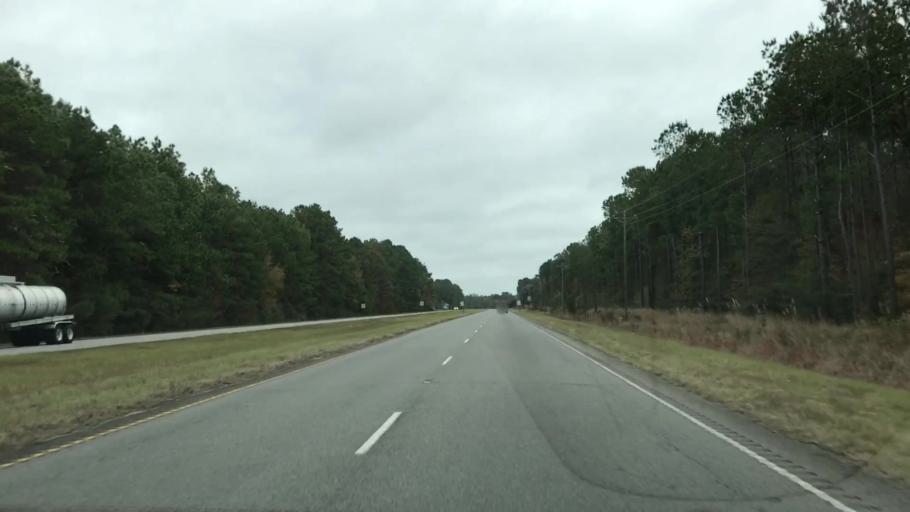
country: US
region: South Carolina
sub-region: Charleston County
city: Awendaw
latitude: 33.0202
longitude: -79.6323
